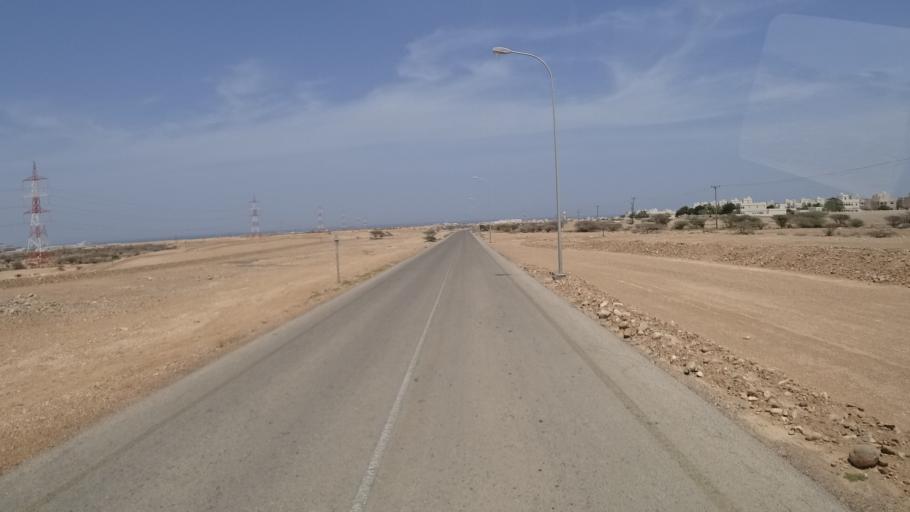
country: OM
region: Ash Sharqiyah
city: Sur
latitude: 22.6085
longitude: 59.4347
